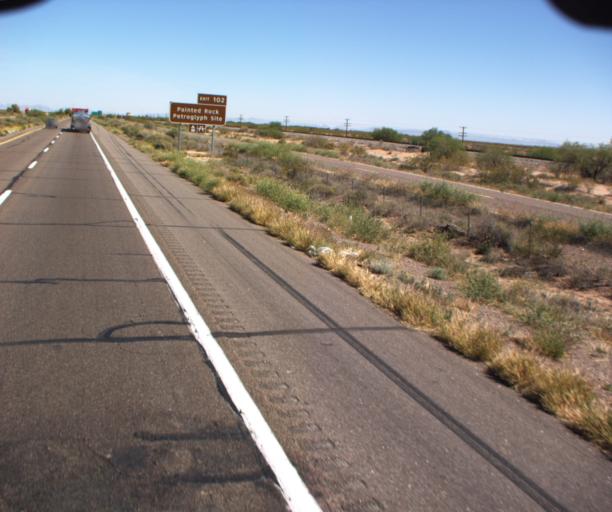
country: US
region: Arizona
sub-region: Maricopa County
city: Gila Bend
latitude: 32.9080
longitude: -112.9771
